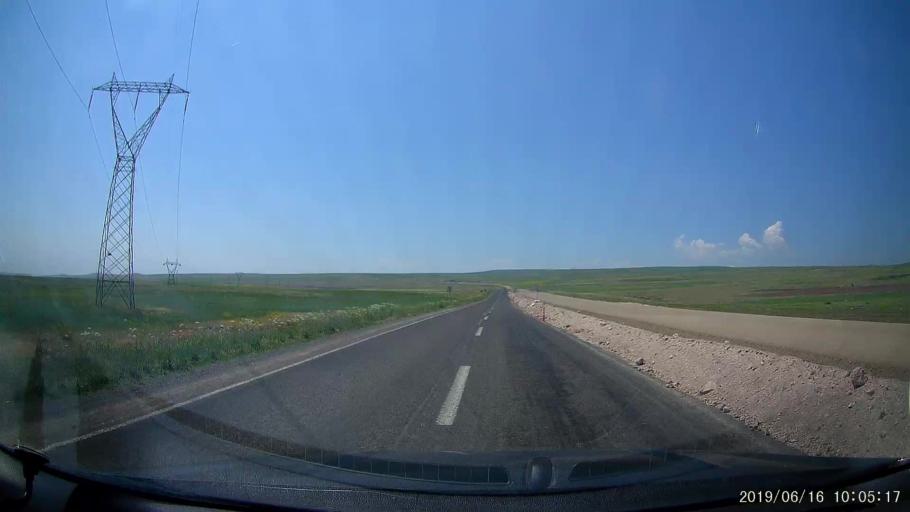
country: TR
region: Kars
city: Digor
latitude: 40.2724
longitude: 43.5380
